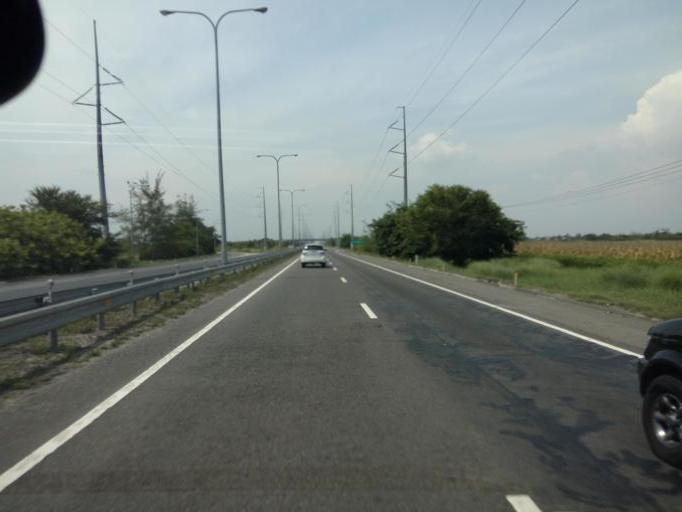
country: PH
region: Central Luzon
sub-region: Province of Tarlac
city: Santo Nino
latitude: 15.3138
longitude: 120.6217
